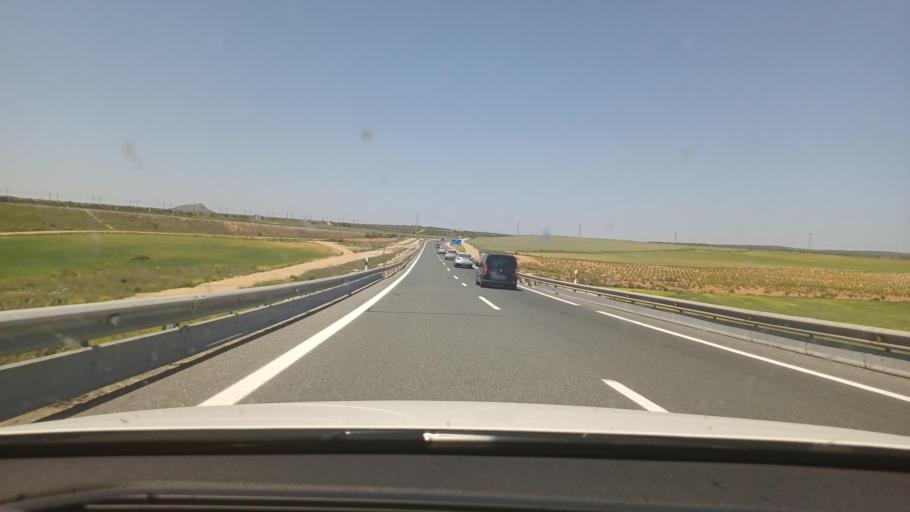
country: ES
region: Castille-La Mancha
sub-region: Provincia de Albacete
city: Alpera
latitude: 38.8785
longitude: -1.2293
